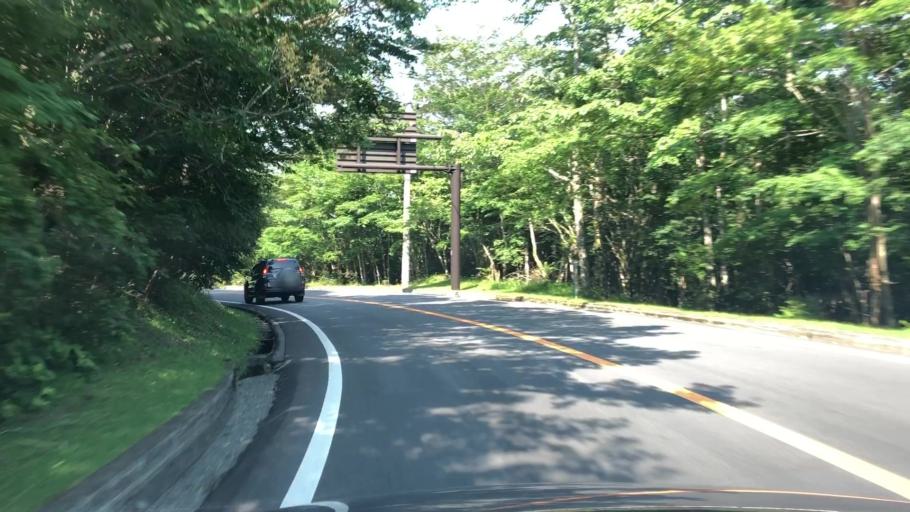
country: JP
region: Shizuoka
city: Gotemba
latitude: 35.3304
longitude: 138.8043
